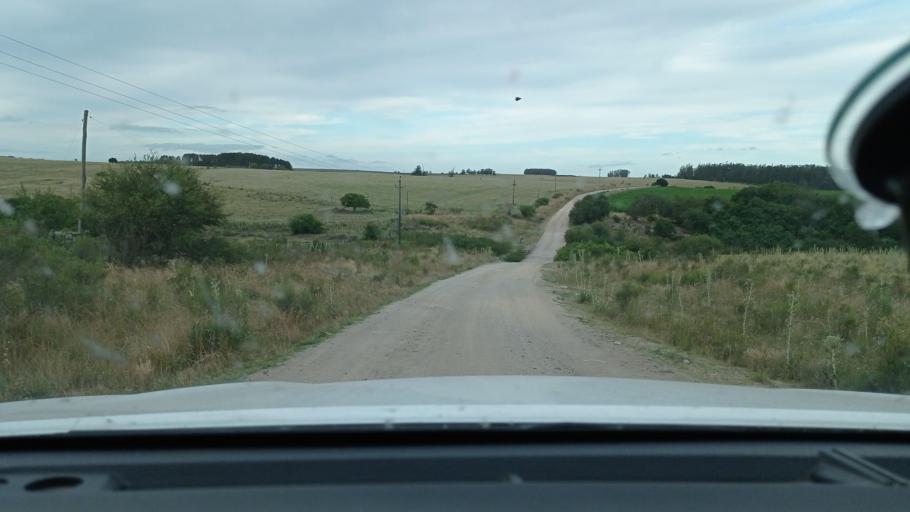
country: UY
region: Florida
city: Casupa
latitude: -34.1007
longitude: -55.7429
